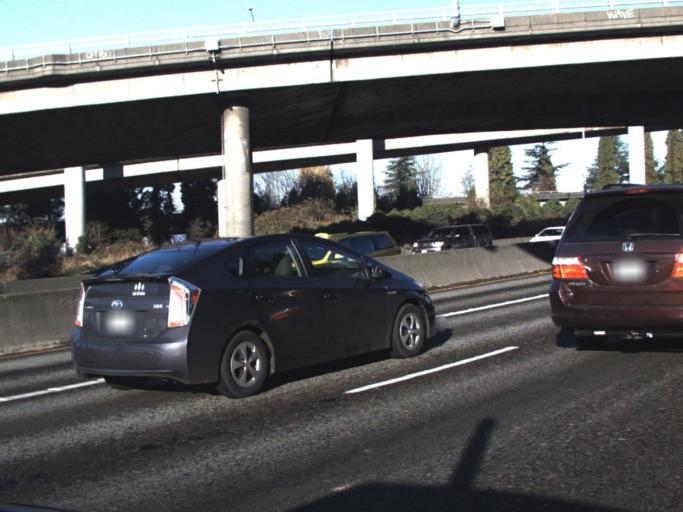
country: US
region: Washington
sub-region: King County
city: Seattle
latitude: 47.5713
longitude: -122.3199
